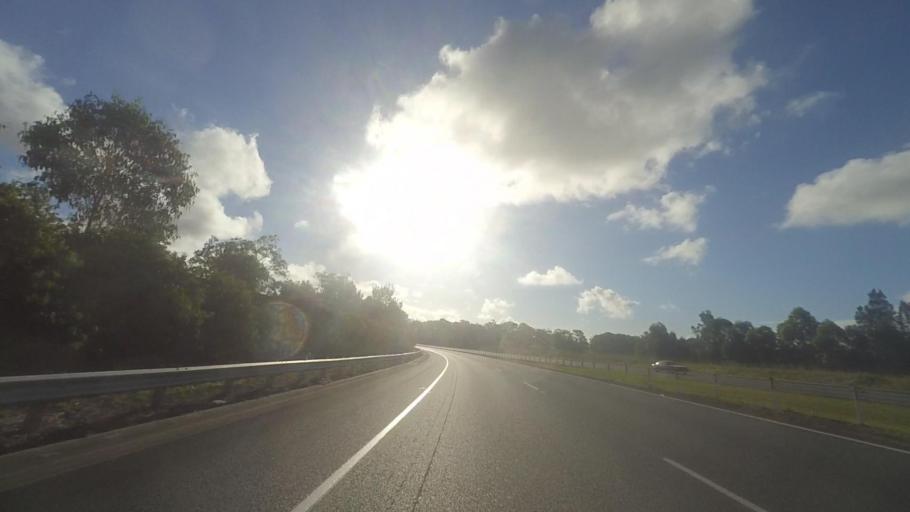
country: AU
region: New South Wales
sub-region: Great Lakes
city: Nabiac
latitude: -32.0924
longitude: 152.3879
